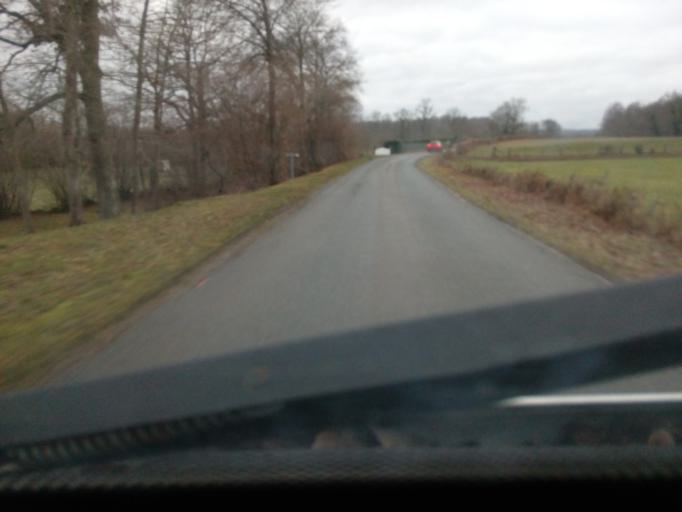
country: FR
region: Limousin
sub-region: Departement de la Creuse
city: Felletin
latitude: 45.8453
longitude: 2.2351
